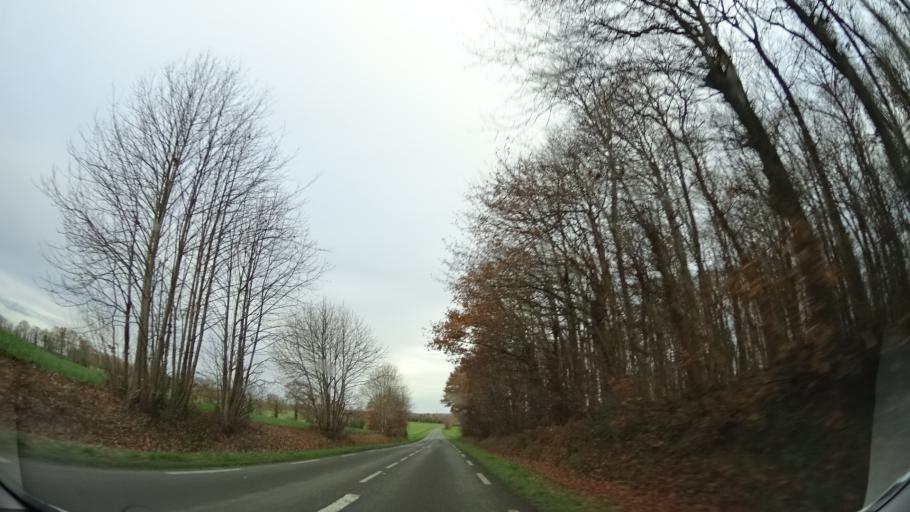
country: FR
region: Brittany
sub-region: Departement des Cotes-d'Armor
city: Evran
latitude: 48.3578
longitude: -1.9690
